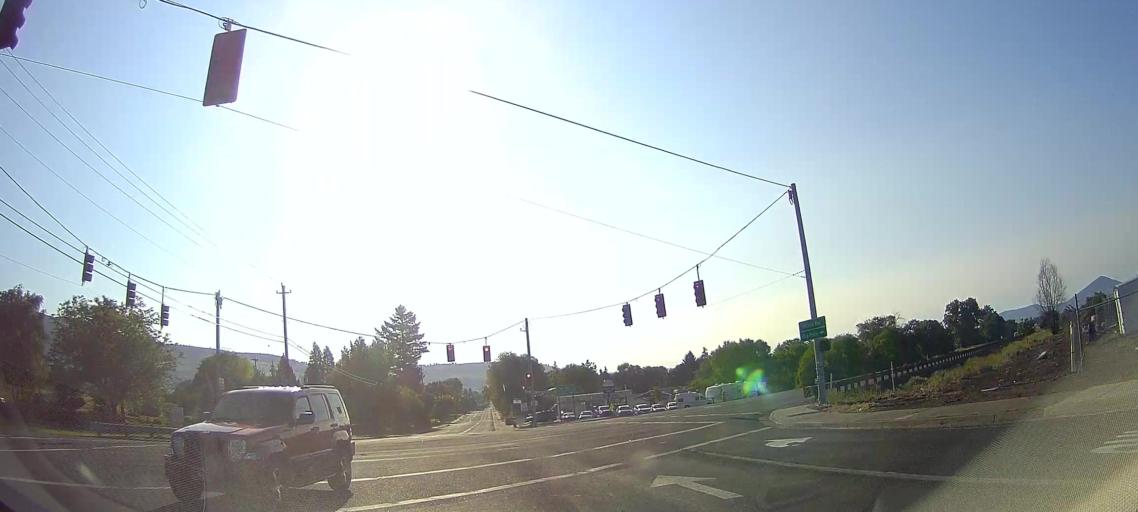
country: US
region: Oregon
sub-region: Klamath County
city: Altamont
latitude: 42.2139
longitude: -121.7439
